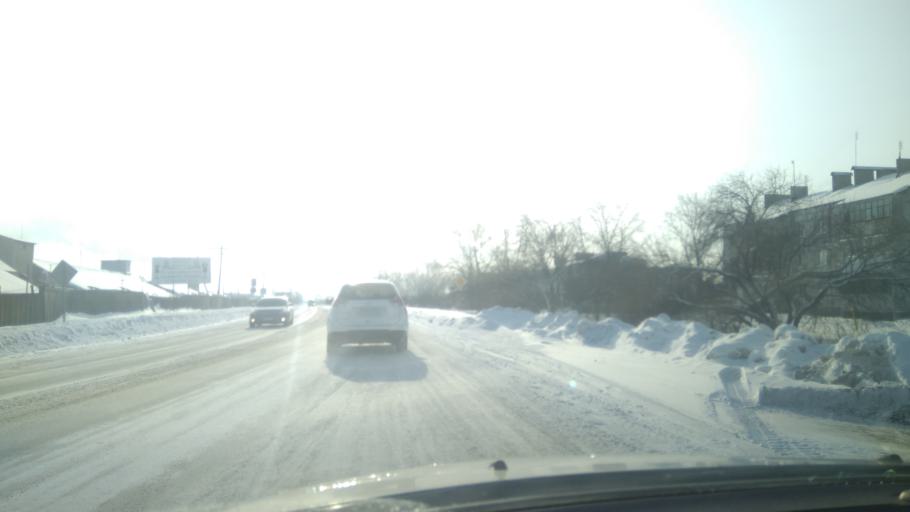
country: RU
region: Sverdlovsk
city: Sukhoy Log
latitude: 56.8909
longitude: 62.0421
